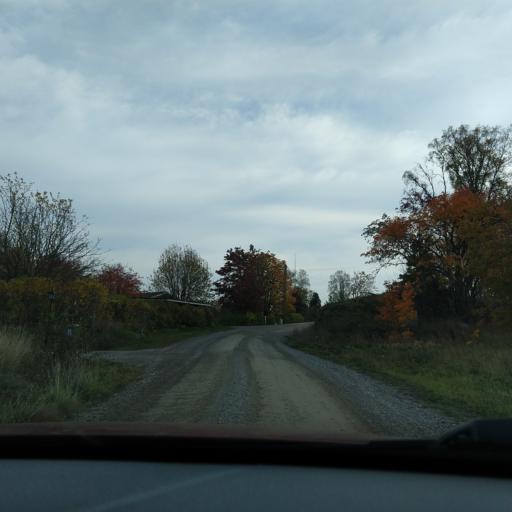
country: SE
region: Stockholm
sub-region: Vallentuna Kommun
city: Vallentuna
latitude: 59.5266
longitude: 18.0143
